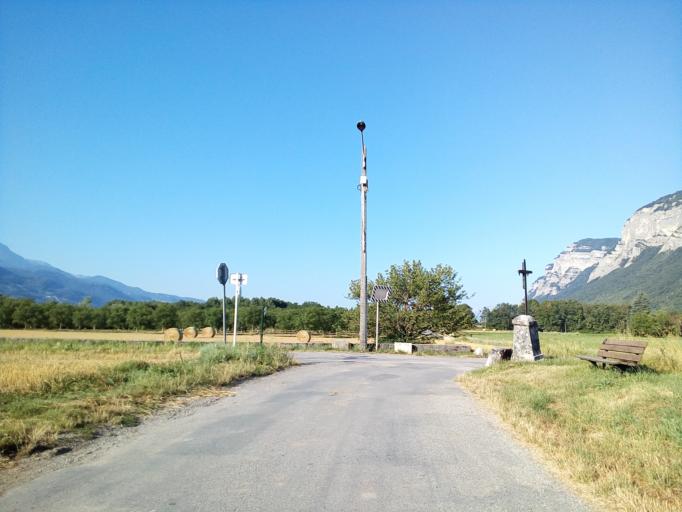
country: FR
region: Rhone-Alpes
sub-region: Departement de l'Isere
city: La Terrasse
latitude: 45.3239
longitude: 5.9378
